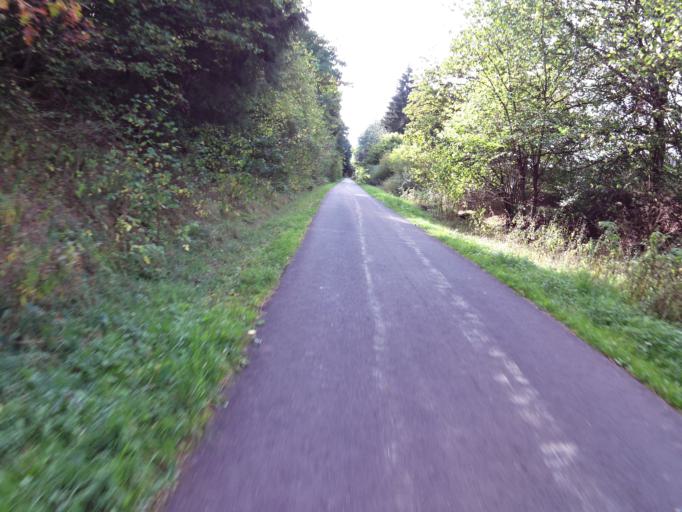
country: DE
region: Rheinland-Pfalz
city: Grosslangenfeld
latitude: 50.2248
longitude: 6.2476
